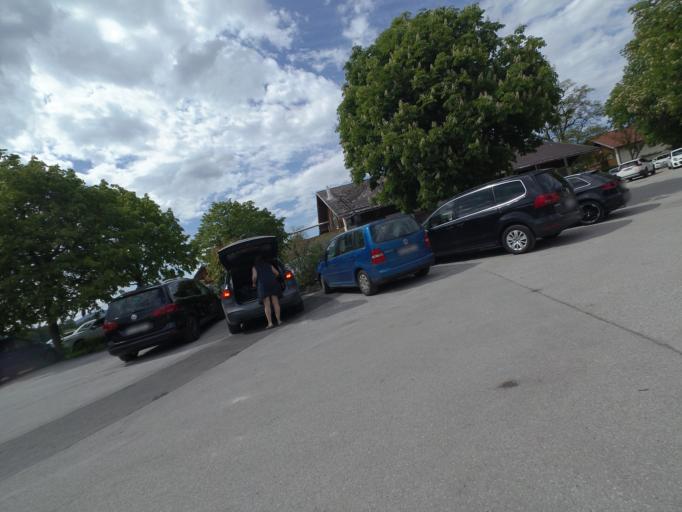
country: AT
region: Salzburg
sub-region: Salzburg Stadt
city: Salzburg
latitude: 47.7758
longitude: 12.9920
